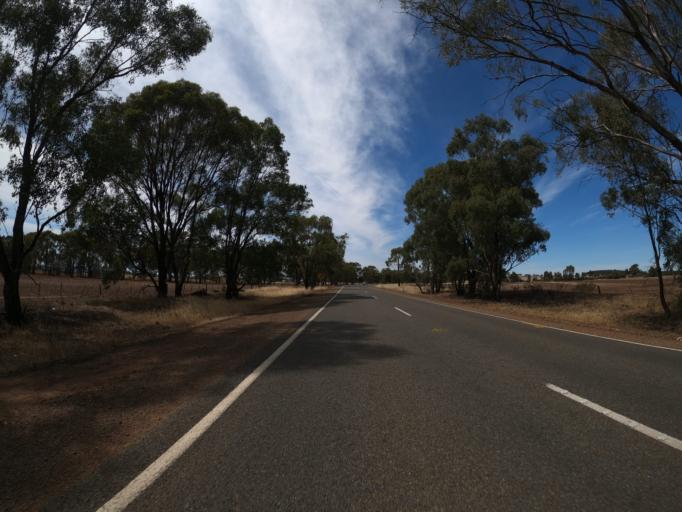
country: AU
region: Victoria
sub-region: Benalla
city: Benalla
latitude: -36.3051
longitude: 145.9570
